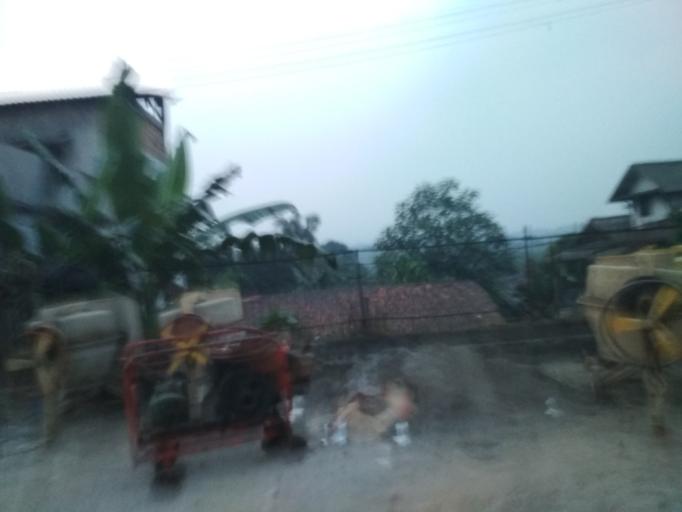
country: ID
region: West Java
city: Caringin
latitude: -6.7129
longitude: 106.8205
